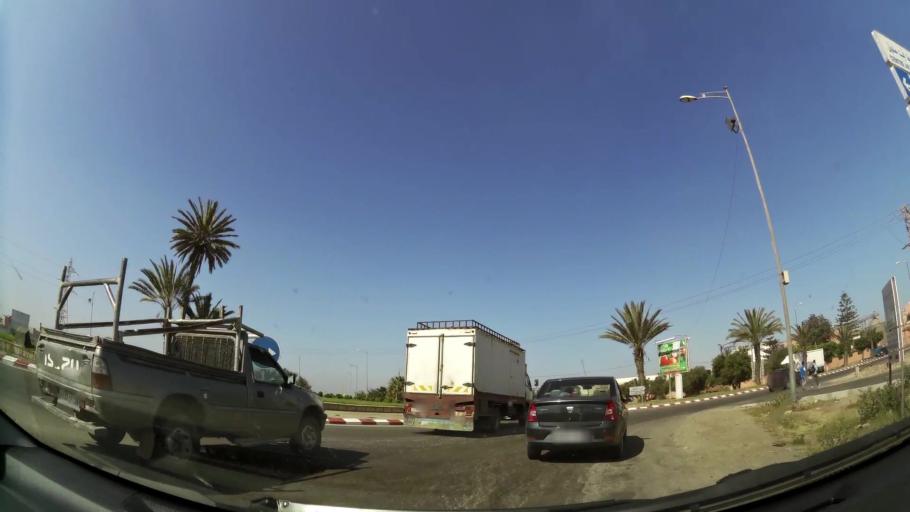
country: MA
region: Souss-Massa-Draa
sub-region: Inezgane-Ait Mellou
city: Inezgane
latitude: 30.3248
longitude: -9.4833
